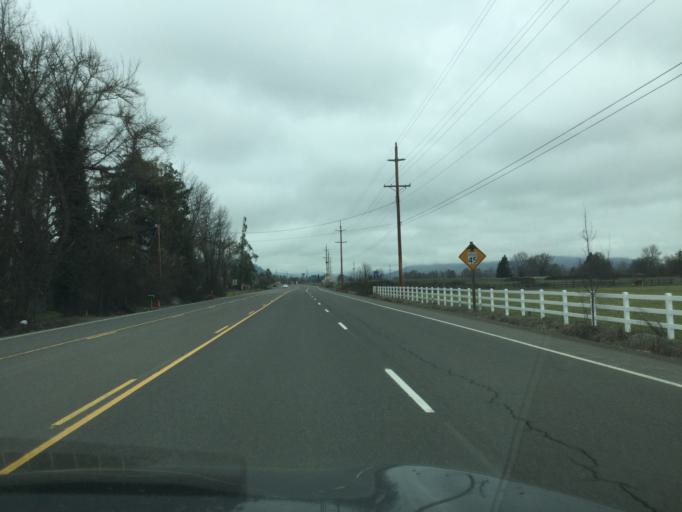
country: US
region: Oregon
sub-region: Jackson County
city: Central Point
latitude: 42.3992
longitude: -122.9408
